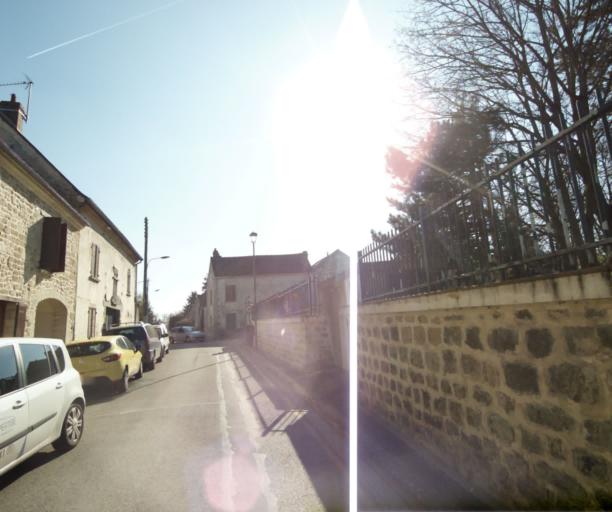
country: FR
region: Ile-de-France
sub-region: Departement du Val-d'Oise
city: Neuville-sur-Oise
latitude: 49.0259
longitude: 2.0574
